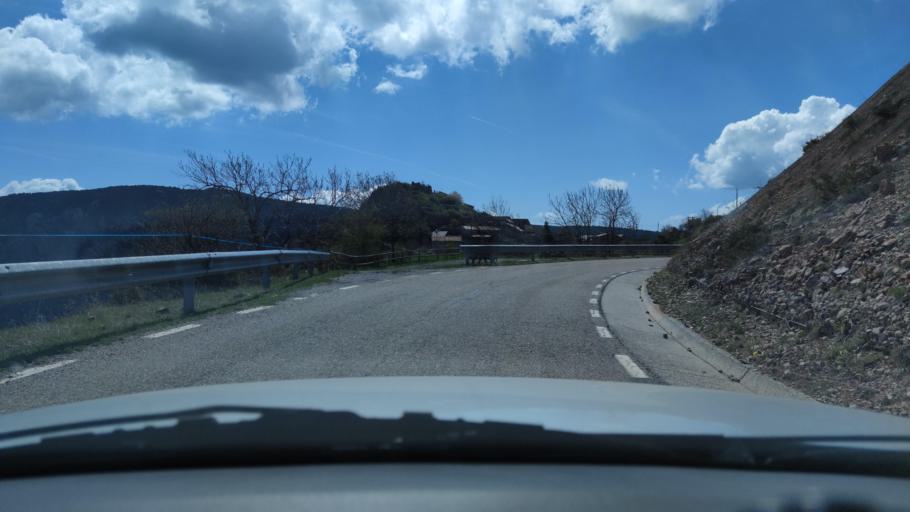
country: ES
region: Catalonia
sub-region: Provincia de Lleida
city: Coll de Nargo
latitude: 42.2885
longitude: 1.2327
